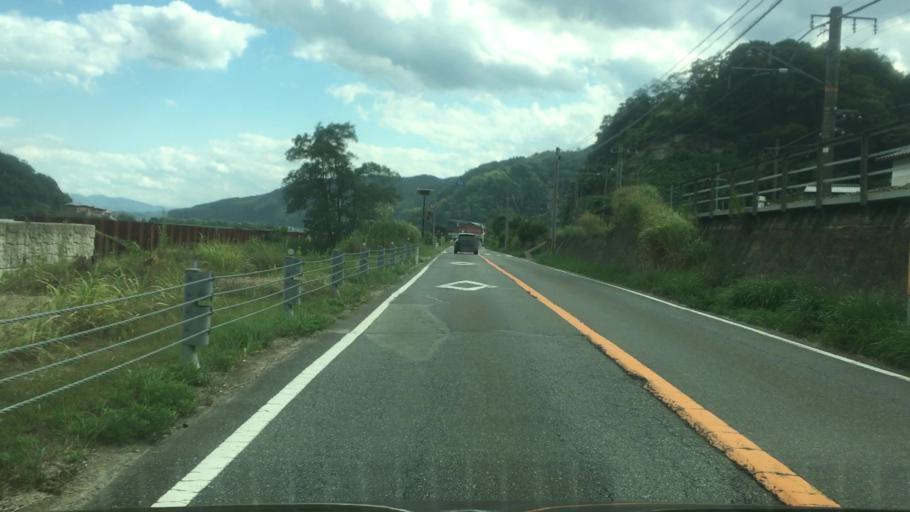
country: JP
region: Hyogo
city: Toyooka
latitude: 35.5969
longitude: 134.8017
